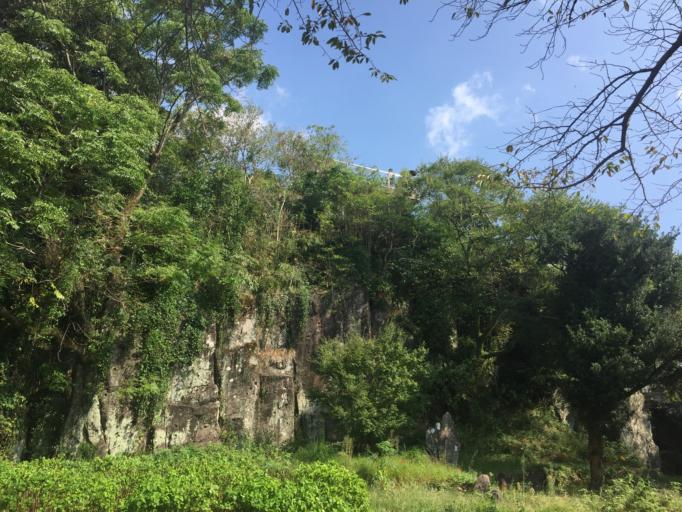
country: JP
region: Nagasaki
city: Nagasaki-shi
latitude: 32.7463
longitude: 129.8858
